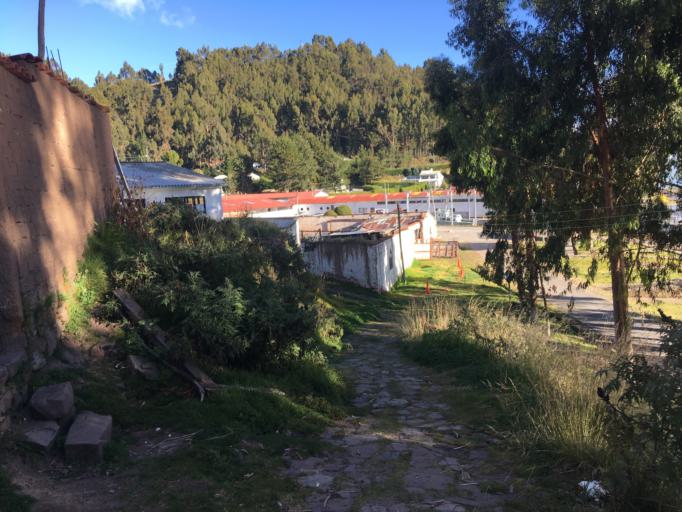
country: BO
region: La Paz
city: San Pedro
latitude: -16.2203
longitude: -68.8542
